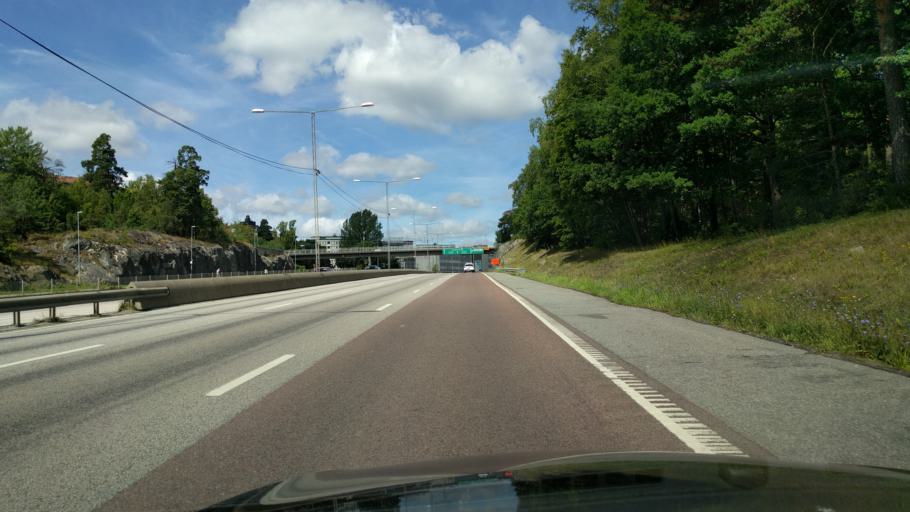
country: SE
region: Stockholm
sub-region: Danderyds Kommun
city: Djursholm
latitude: 59.3947
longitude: 18.0414
